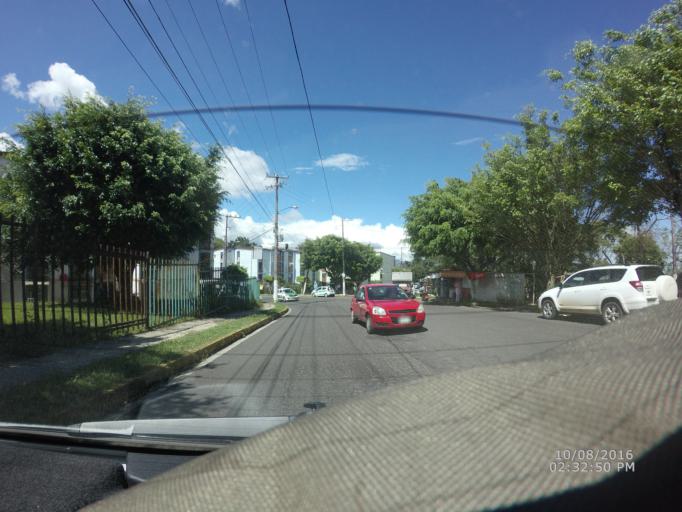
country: MX
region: Veracruz
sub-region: Xalapa
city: Lomas Verdes
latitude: 19.5129
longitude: -96.9040
